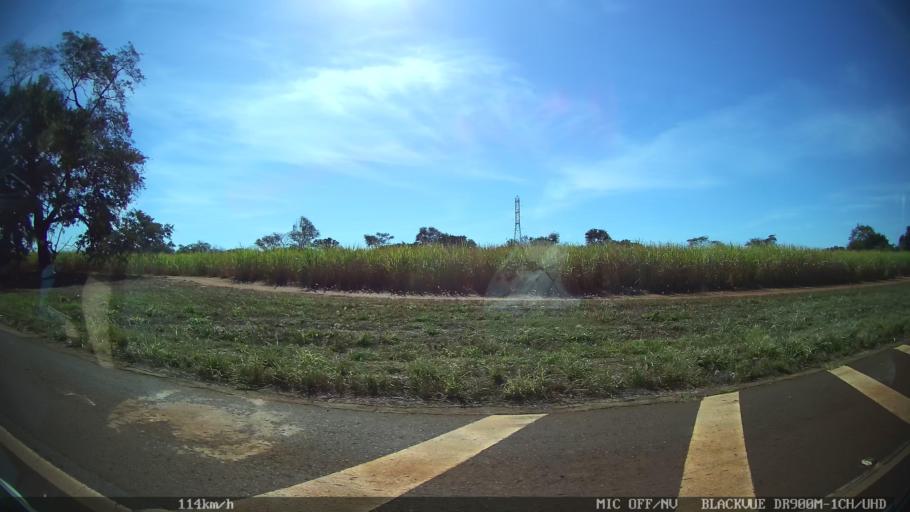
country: BR
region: Sao Paulo
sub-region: Guaira
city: Guaira
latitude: -20.4453
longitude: -48.2230
